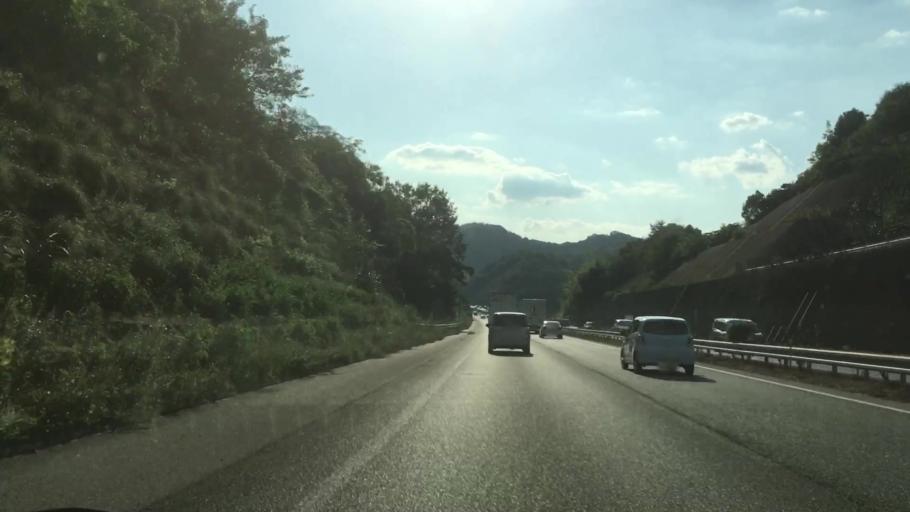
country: JP
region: Yamaguchi
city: Tokuyama
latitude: 34.0799
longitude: 131.7252
